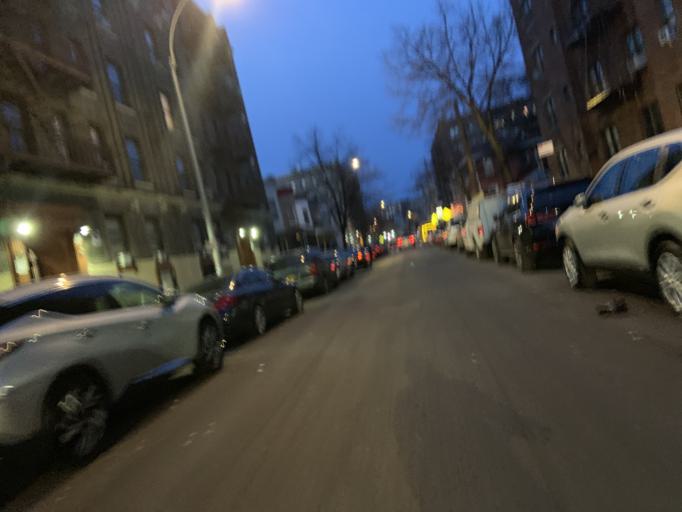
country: US
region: New York
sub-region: Bronx
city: The Bronx
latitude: 40.8677
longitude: -73.8904
